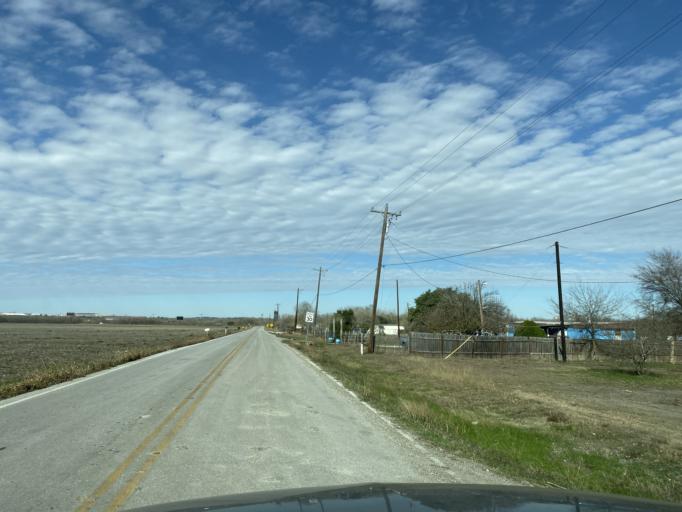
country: US
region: Texas
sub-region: Travis County
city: Onion Creek
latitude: 30.0857
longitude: -97.7046
